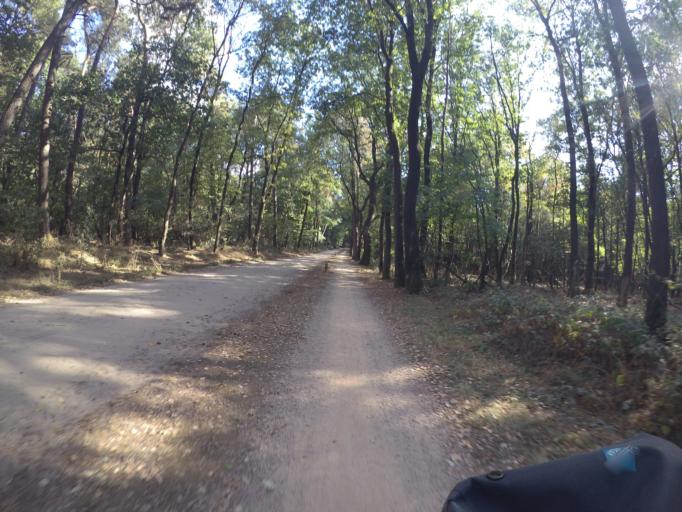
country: NL
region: Overijssel
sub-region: Gemeente Hof van Twente
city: Markelo
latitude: 52.2714
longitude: 6.5141
